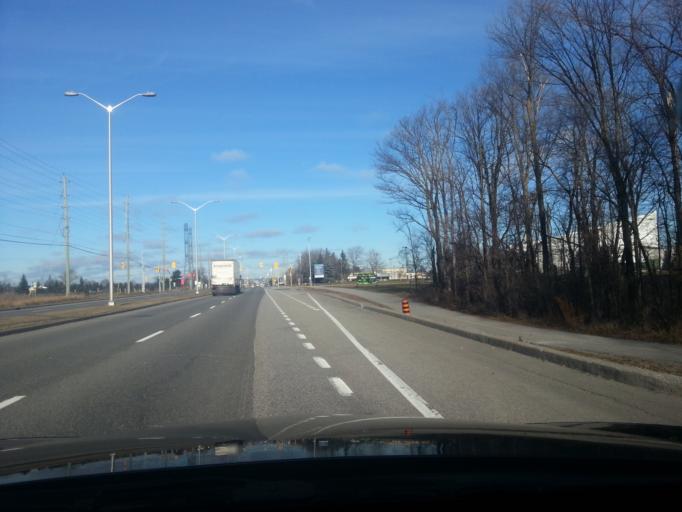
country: CA
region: Ontario
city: Bells Corners
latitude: 45.3244
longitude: -75.7461
